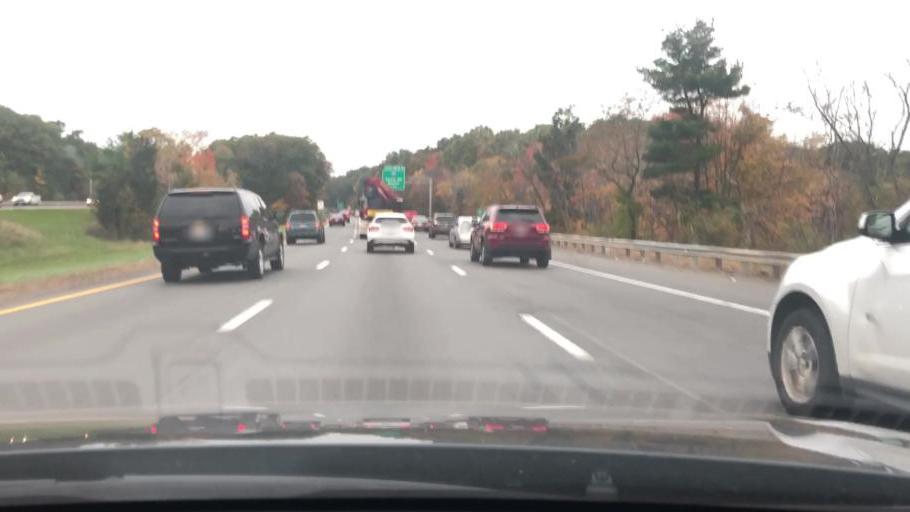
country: US
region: Massachusetts
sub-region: Essex County
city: Lawrence
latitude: 42.6744
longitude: -71.1738
